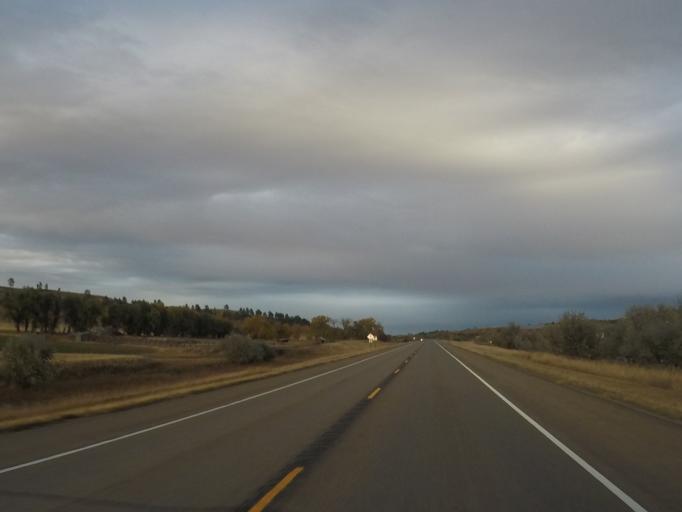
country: US
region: Montana
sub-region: Golden Valley County
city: Ryegate
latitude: 46.2970
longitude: -109.2385
